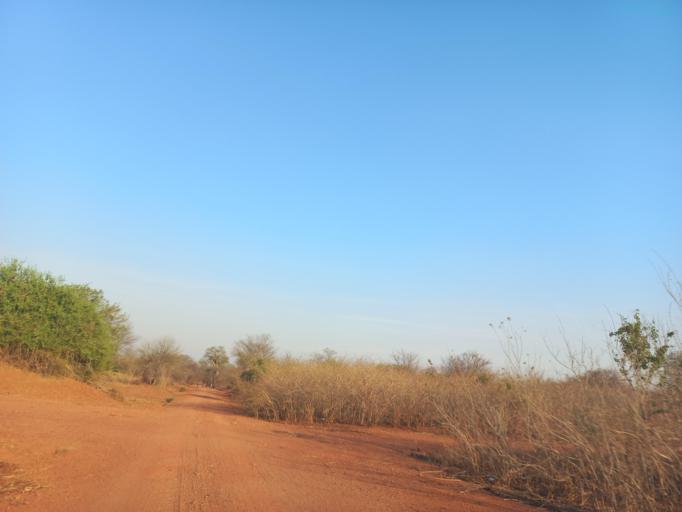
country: ZM
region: Lusaka
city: Luangwa
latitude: -15.4460
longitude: 30.3689
